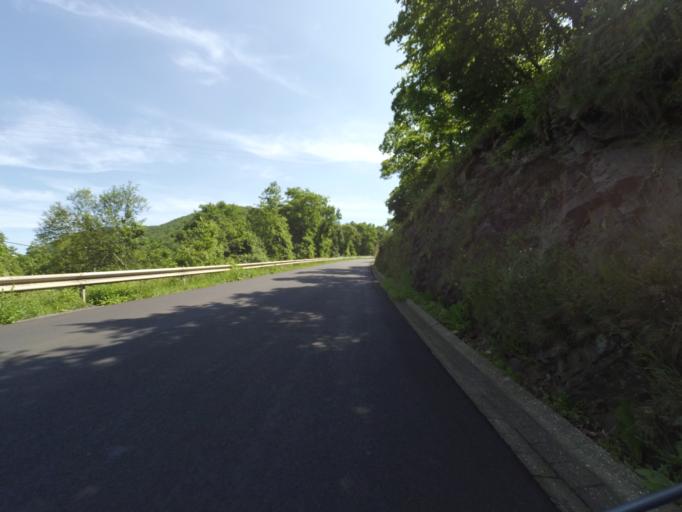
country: DE
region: Rheinland-Pfalz
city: Reudelsterz
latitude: 50.2958
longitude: 7.1449
